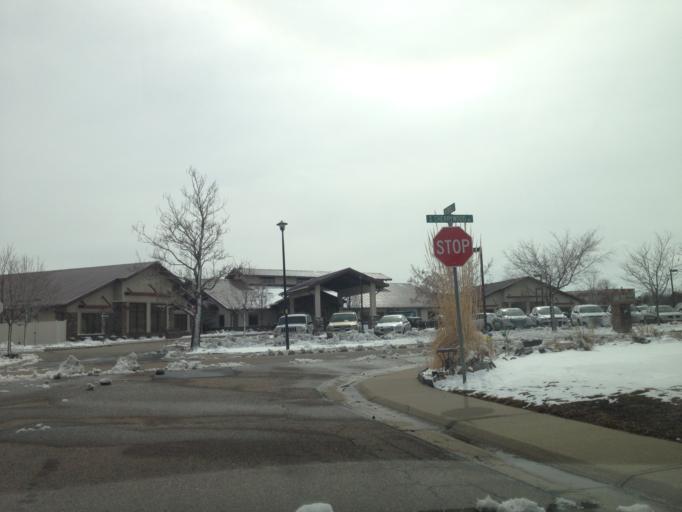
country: US
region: Colorado
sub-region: Boulder County
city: Lafayette
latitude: 39.9740
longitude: -105.0922
